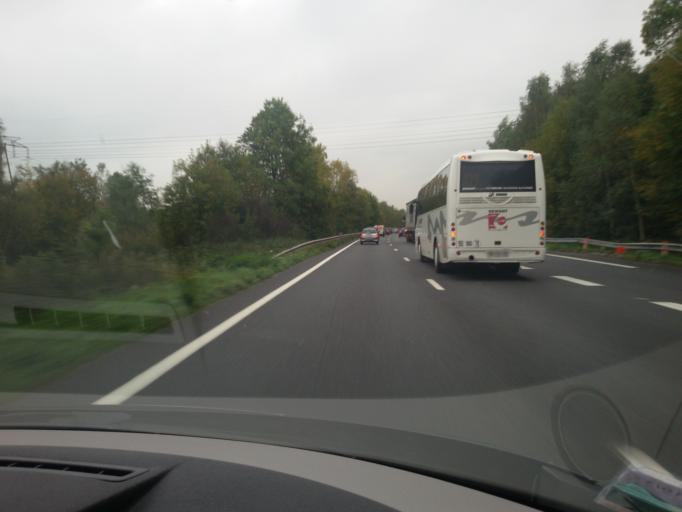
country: FR
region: Ile-de-France
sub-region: Departement de l'Essonne
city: Les Ulis
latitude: 48.6531
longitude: 2.1798
